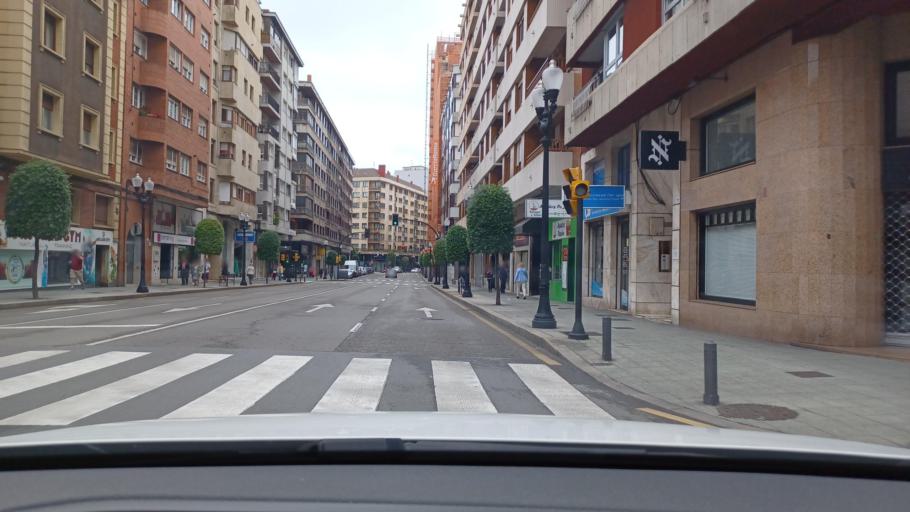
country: ES
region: Asturias
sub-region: Province of Asturias
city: Gijon
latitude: 43.5360
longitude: -5.6531
